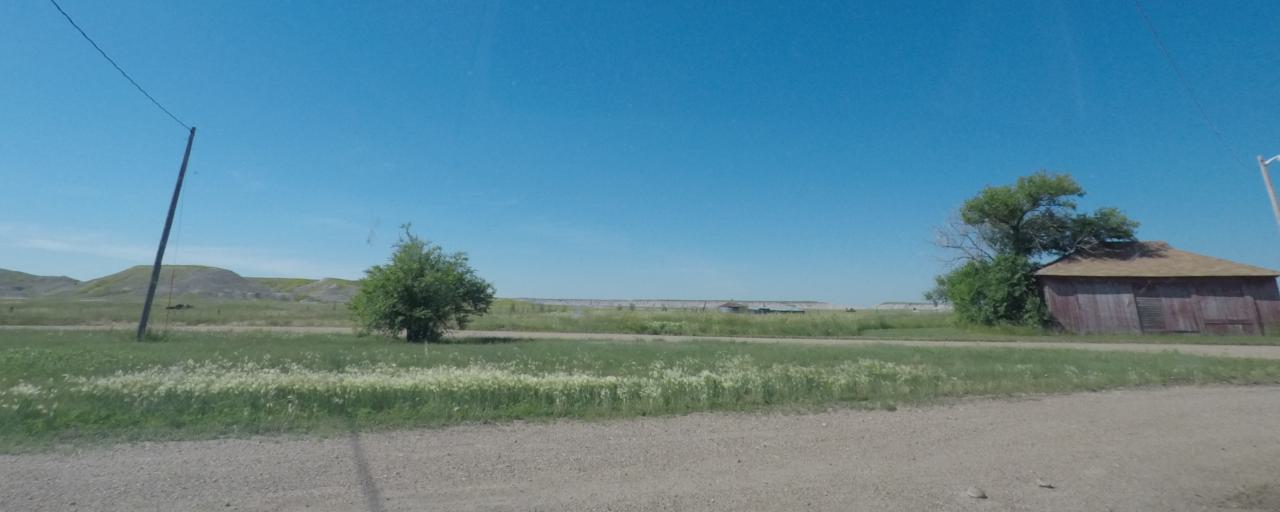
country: US
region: South Dakota
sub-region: Shannon County
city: Porcupine
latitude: 43.7787
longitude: -102.5541
